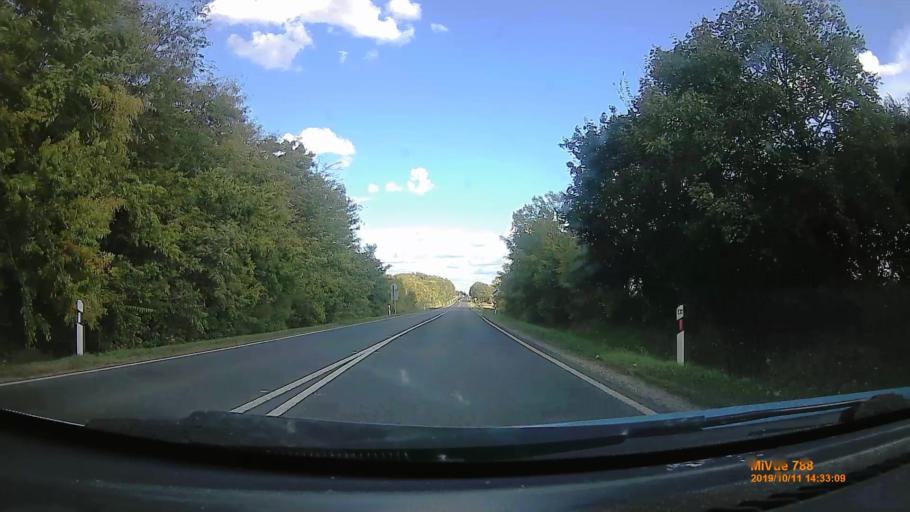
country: HU
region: Hajdu-Bihar
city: Ebes
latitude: 47.5622
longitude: 21.4510
